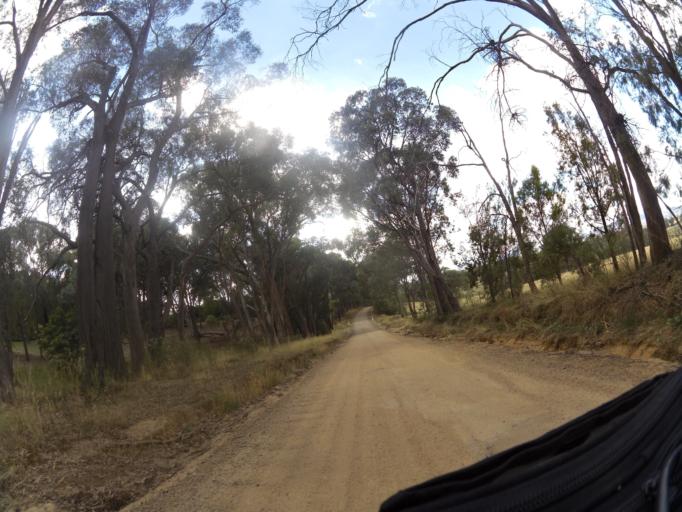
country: AU
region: Victoria
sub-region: Benalla
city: Benalla
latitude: -36.7819
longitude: 145.9897
